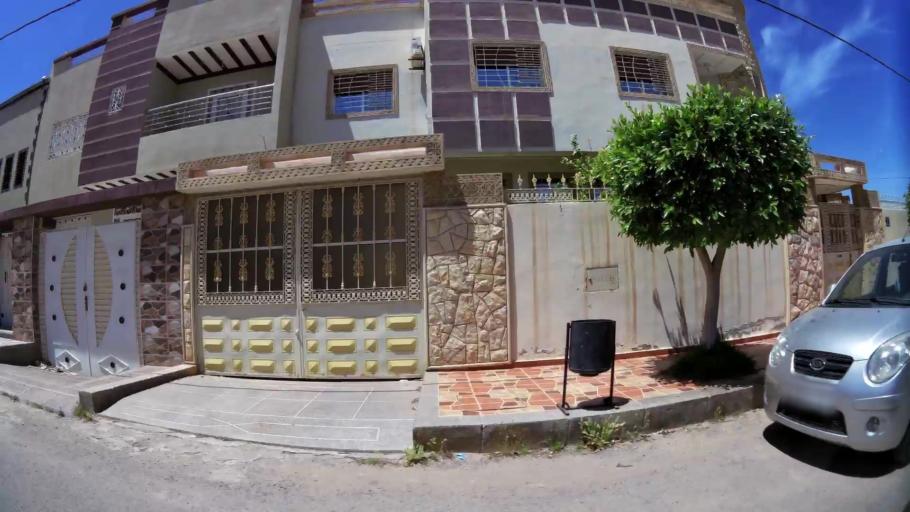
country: MA
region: Oriental
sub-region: Oujda-Angad
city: Oujda
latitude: 34.6598
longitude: -1.9446
